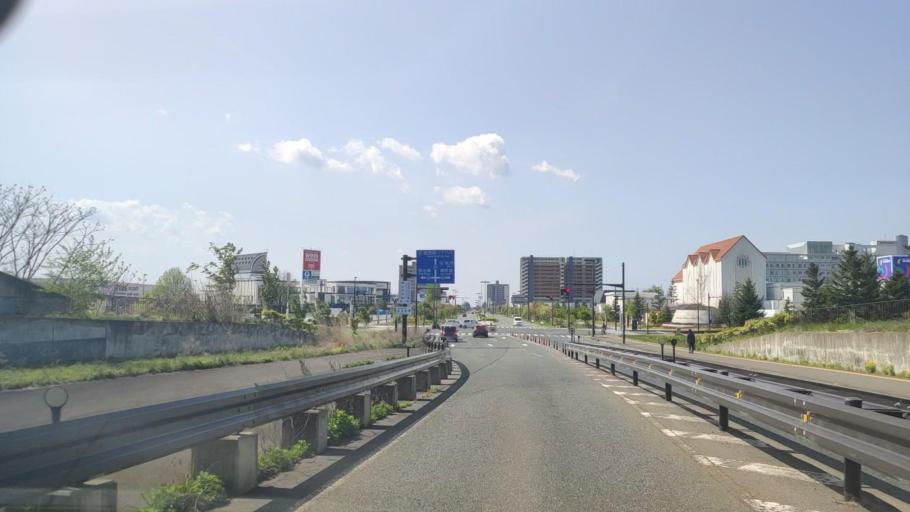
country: JP
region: Iwate
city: Morioka-shi
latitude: 39.6927
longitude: 141.1271
